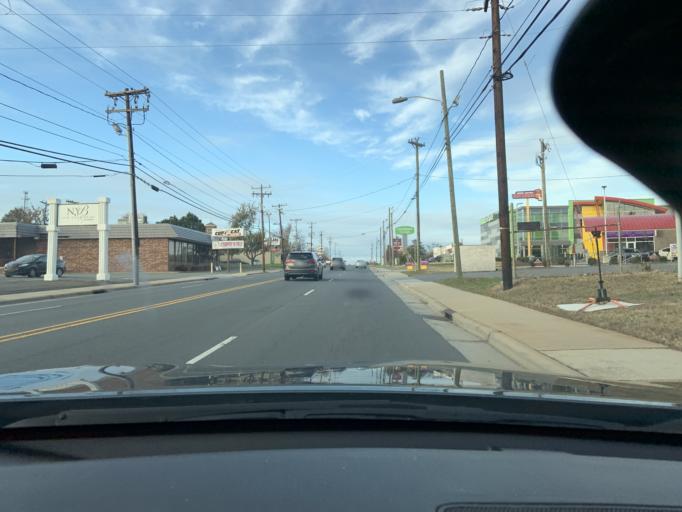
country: US
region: North Carolina
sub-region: Mecklenburg County
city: Charlotte
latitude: 35.1780
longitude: -80.8758
